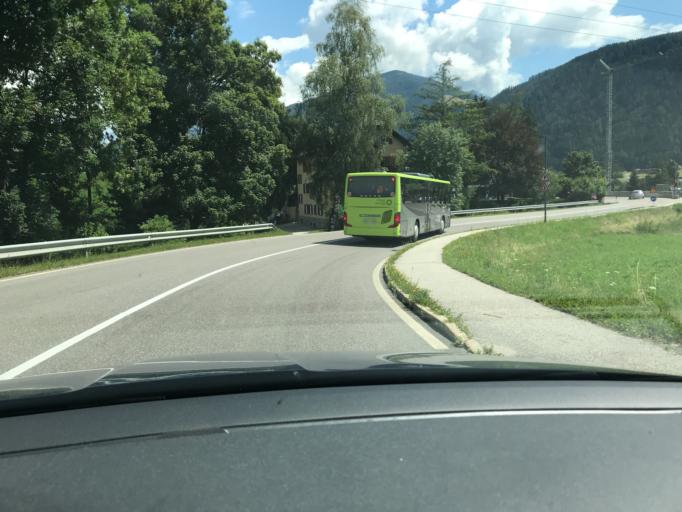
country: IT
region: Trentino-Alto Adige
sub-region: Bolzano
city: Valdaora di Mezzo
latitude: 46.7711
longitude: 12.0310
